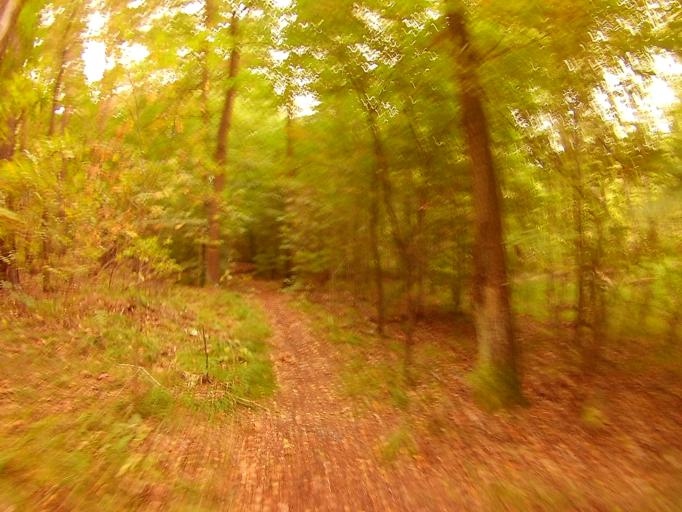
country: DE
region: Brandenburg
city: Zeuthen
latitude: 52.4018
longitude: 13.6175
